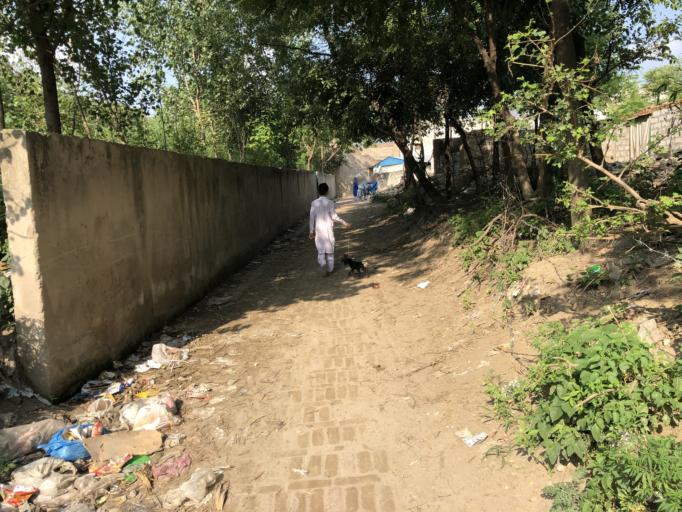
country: PK
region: Khyber Pakhtunkhwa
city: Daggar
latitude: 34.5973
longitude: 72.4505
